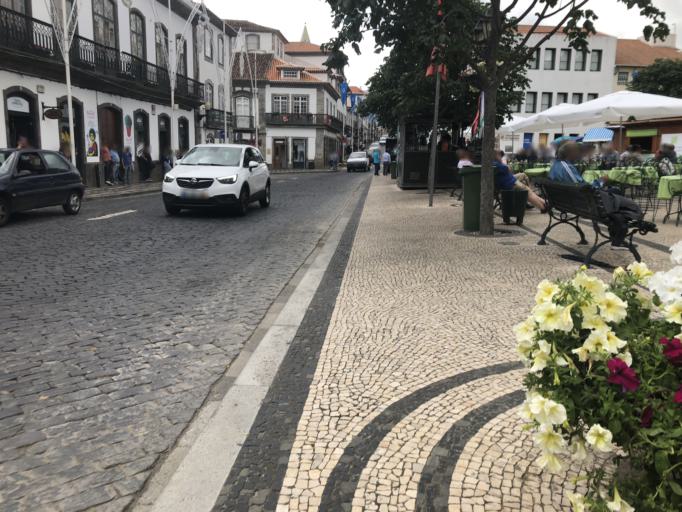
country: PT
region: Azores
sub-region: Angra do Heroismo
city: Angra do Heroismo
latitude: 38.6558
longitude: -27.2184
